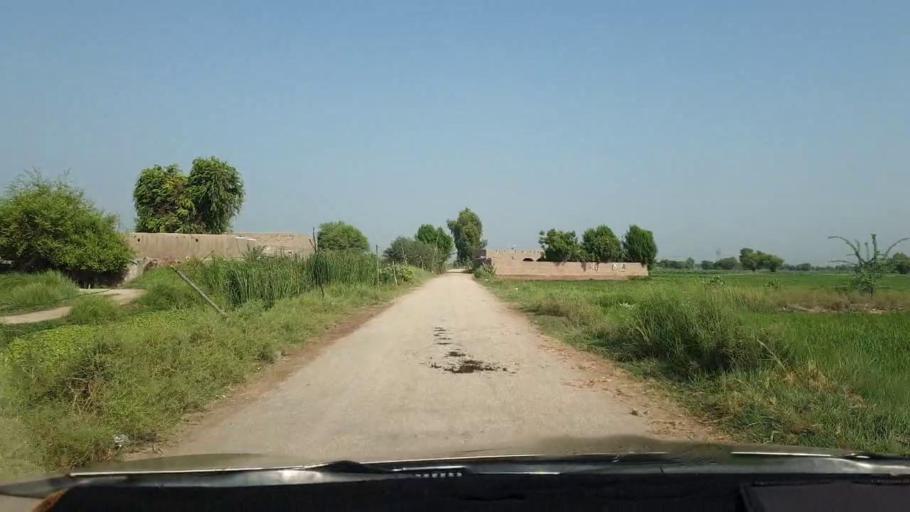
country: PK
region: Sindh
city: Larkana
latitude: 27.6309
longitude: 68.2397
